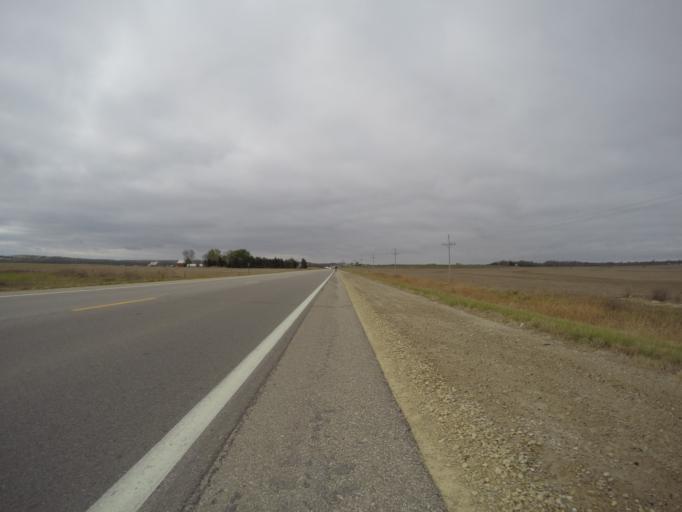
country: US
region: Kansas
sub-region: Pottawatomie County
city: Wamego
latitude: 39.1699
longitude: -96.3055
